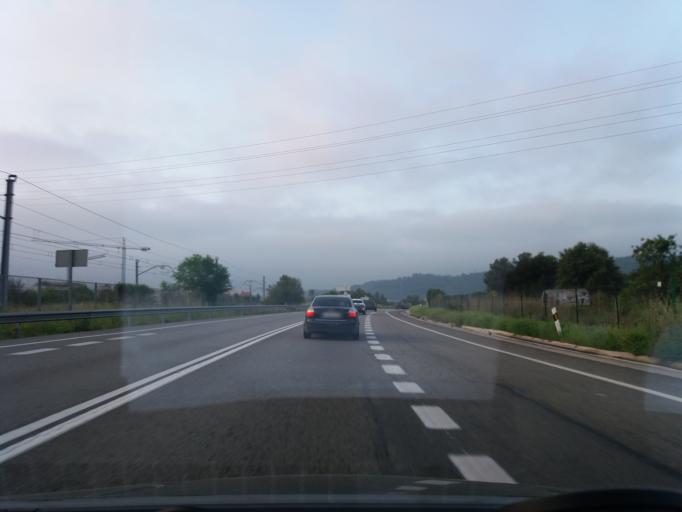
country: ES
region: Catalonia
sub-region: Provincia de Barcelona
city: Olesa de Montserrat
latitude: 41.5505
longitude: 1.8809
